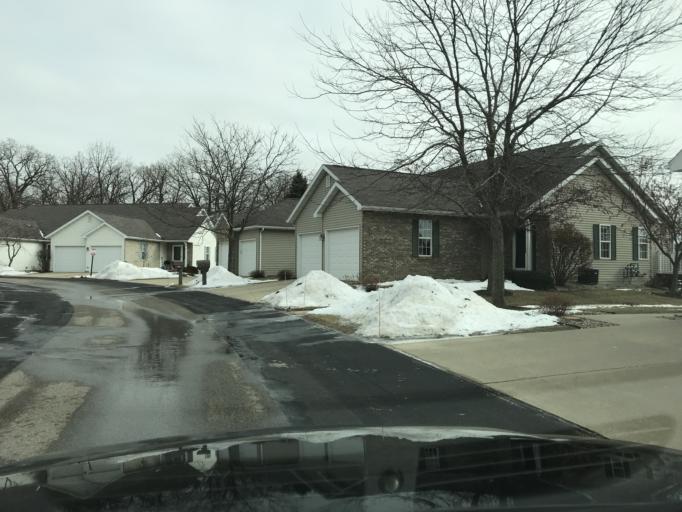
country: US
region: Wisconsin
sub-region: Dane County
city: Monona
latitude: 43.0859
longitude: -89.2702
